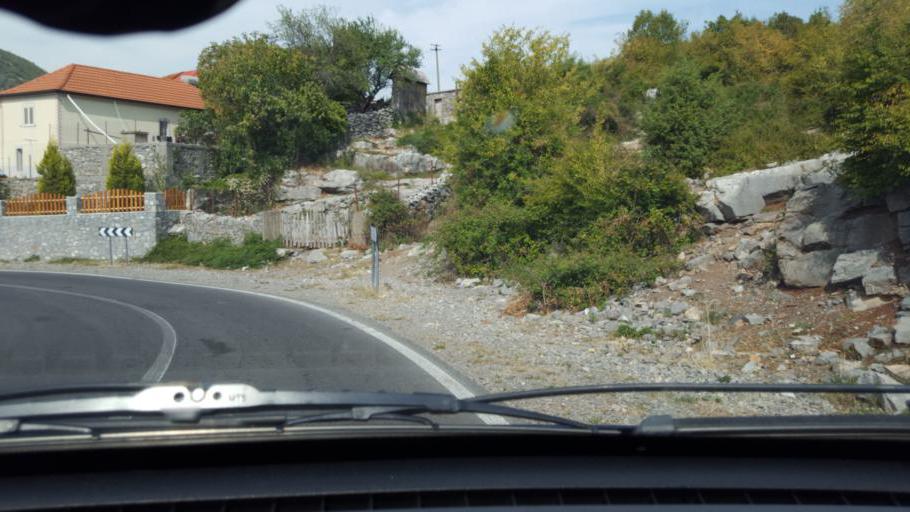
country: AL
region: Shkoder
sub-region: Rrethi i Malesia e Madhe
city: Kastrat
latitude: 42.3833
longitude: 19.4945
